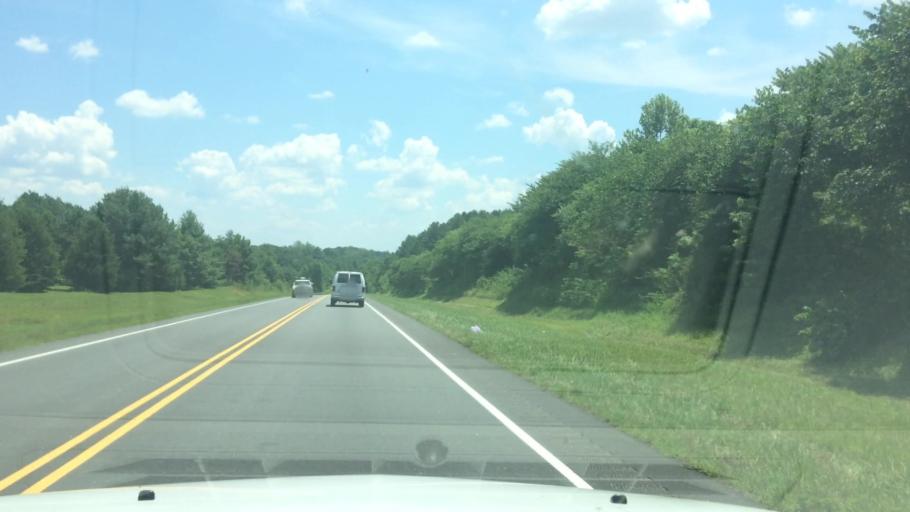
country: US
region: North Carolina
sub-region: Alexander County
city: Stony Point
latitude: 35.8497
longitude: -81.0360
